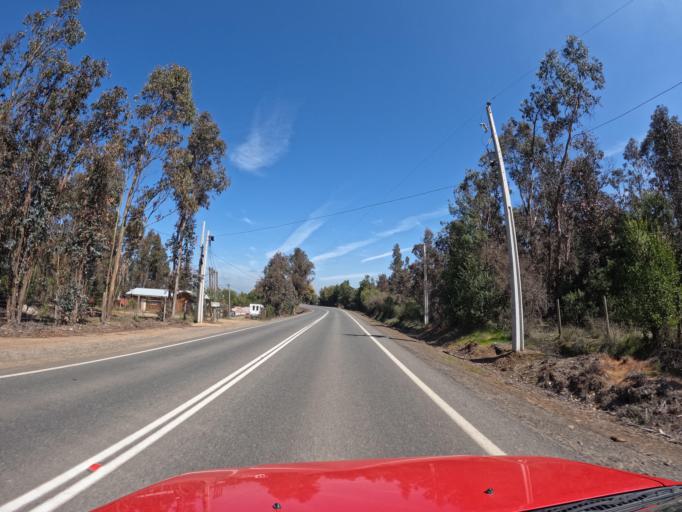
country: CL
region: Maule
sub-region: Provincia de Talca
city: San Clemente
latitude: -35.4451
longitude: -71.2676
